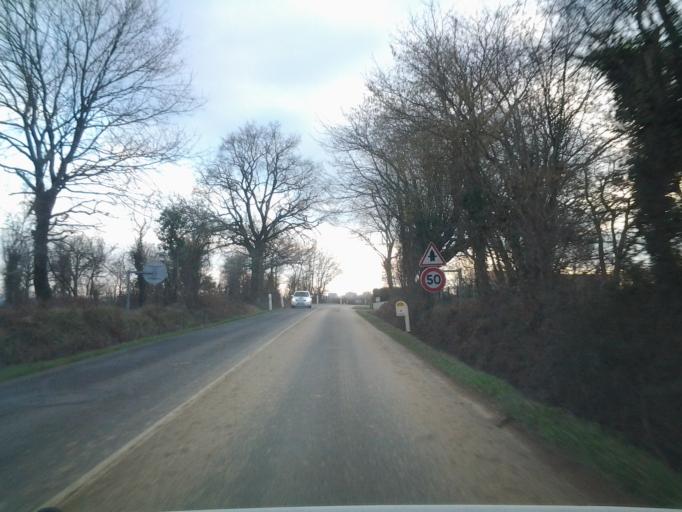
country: FR
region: Pays de la Loire
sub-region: Departement de la Vendee
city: La Roche-sur-Yon
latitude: 46.6994
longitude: -1.4205
